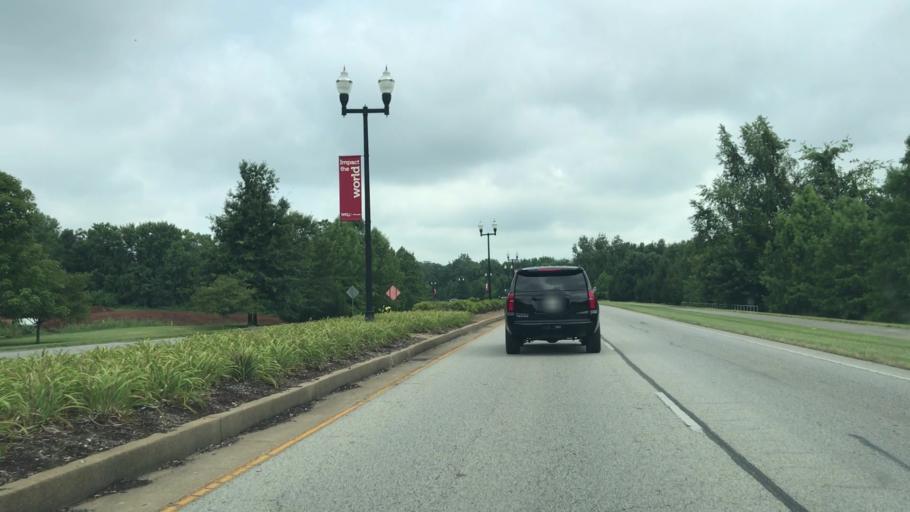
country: US
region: Kentucky
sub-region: Warren County
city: Bowling Green
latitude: 36.9825
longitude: -86.3969
